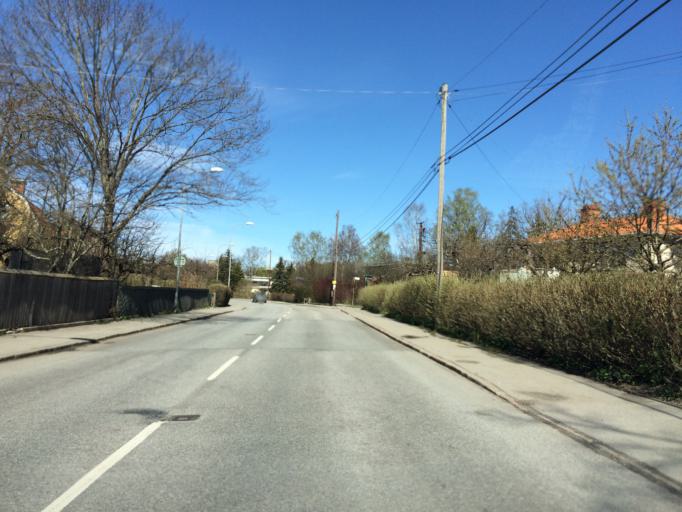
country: SE
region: Stockholm
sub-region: Huddinge Kommun
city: Segeltorp
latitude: 59.2780
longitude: 17.9620
